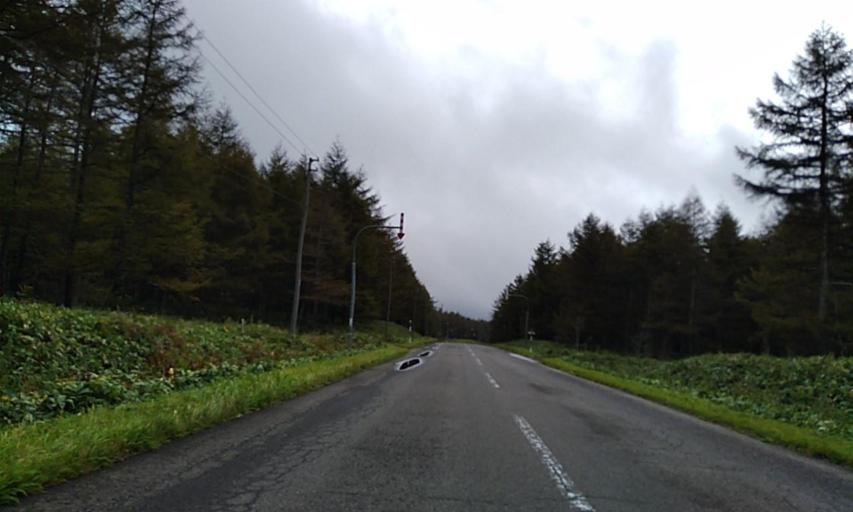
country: JP
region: Hokkaido
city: Abashiri
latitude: 43.6098
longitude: 144.6030
